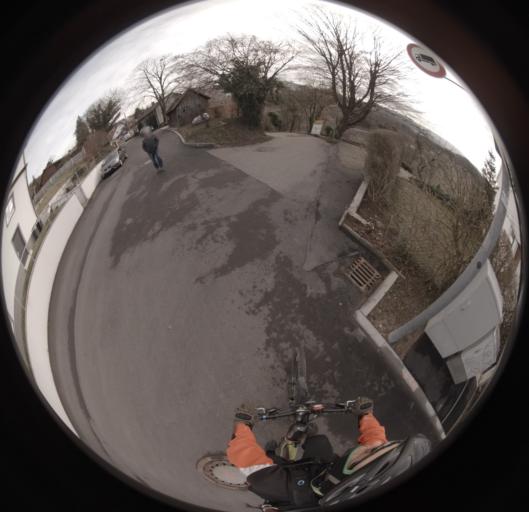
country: DE
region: Baden-Wuerttemberg
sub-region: Regierungsbezirk Stuttgart
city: Ottenbach
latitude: 48.7389
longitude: 9.7146
